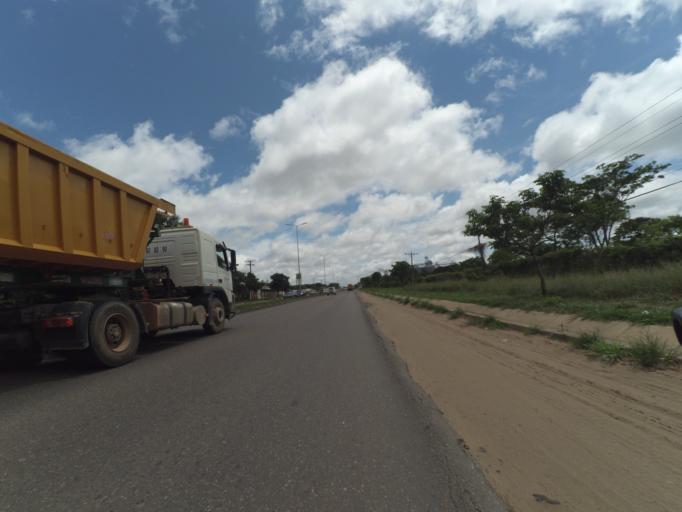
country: BO
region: Santa Cruz
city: Santa Cruz de la Sierra
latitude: -17.8612
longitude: -63.2640
